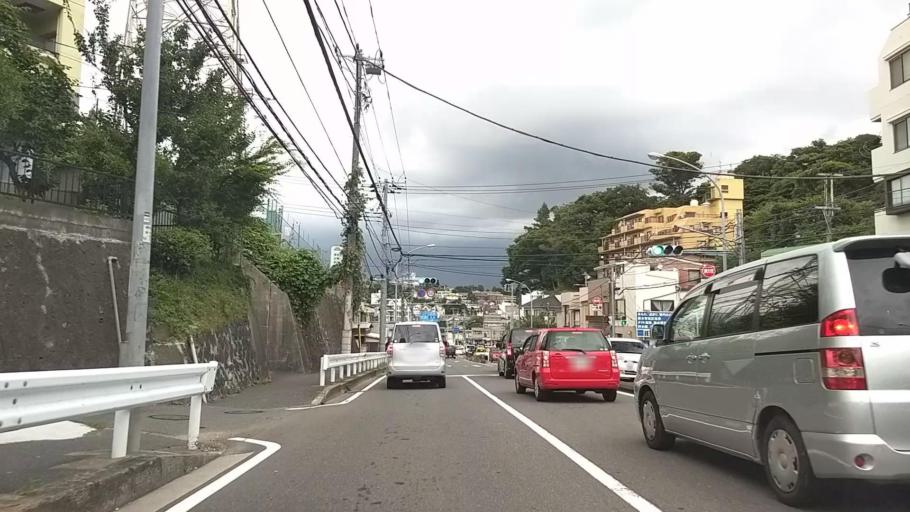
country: JP
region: Kanagawa
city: Yokohama
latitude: 35.4415
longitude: 139.5960
